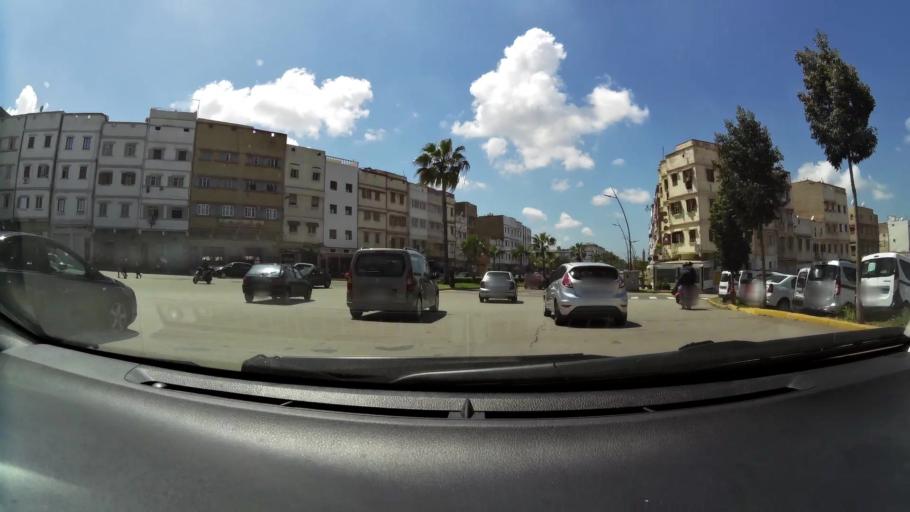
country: MA
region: Grand Casablanca
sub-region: Casablanca
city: Casablanca
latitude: 33.5571
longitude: -7.5806
